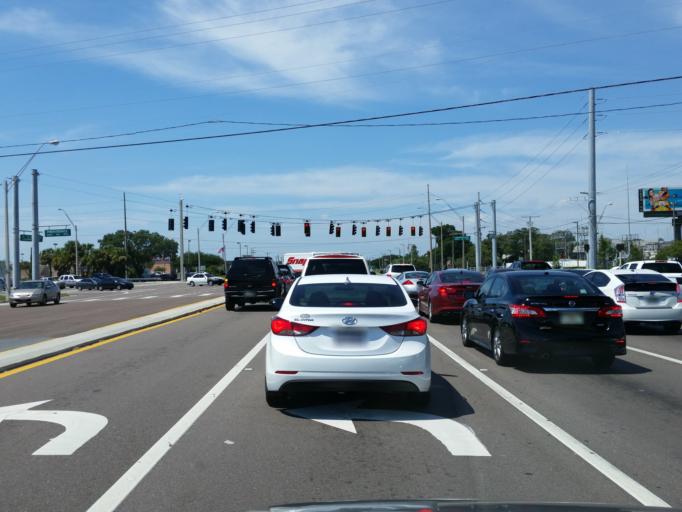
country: US
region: Florida
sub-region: Hillsborough County
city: Brandon
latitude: 27.9233
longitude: -82.3171
